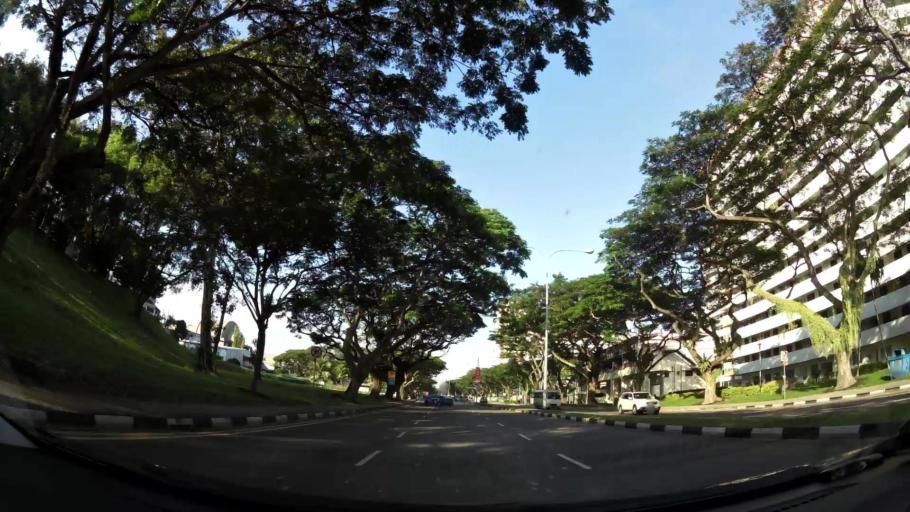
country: SG
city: Singapore
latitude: 1.3201
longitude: 103.9372
